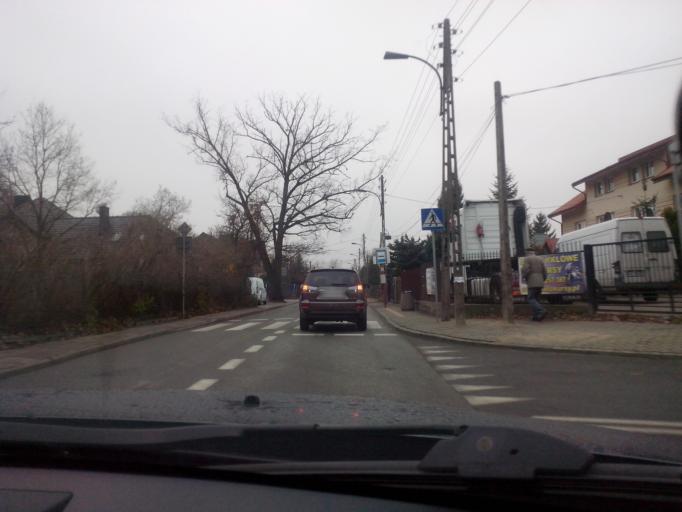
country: PL
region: Masovian Voivodeship
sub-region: Warszawa
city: Bialoleka
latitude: 52.3377
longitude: 20.9654
